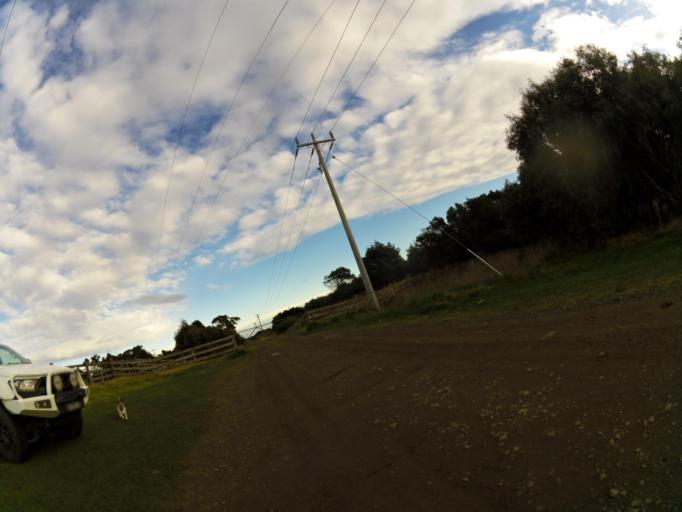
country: AU
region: Victoria
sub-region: Bass Coast
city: North Wonthaggi
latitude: -38.6099
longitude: 145.5674
